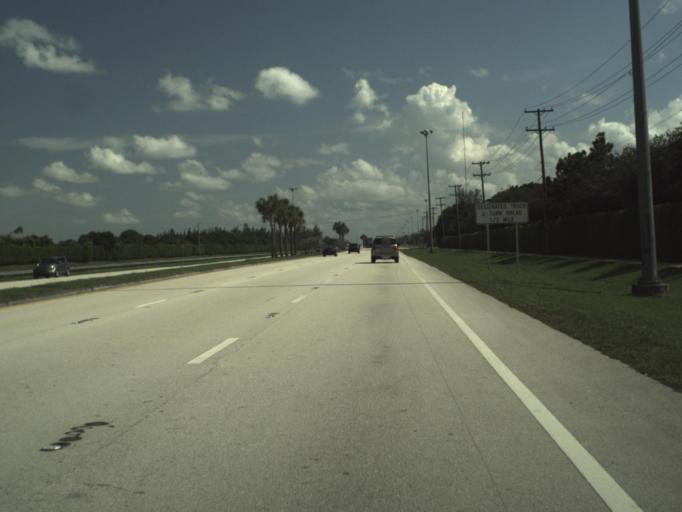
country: US
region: Florida
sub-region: Palm Beach County
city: Wellington
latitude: 26.6101
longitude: -80.2053
